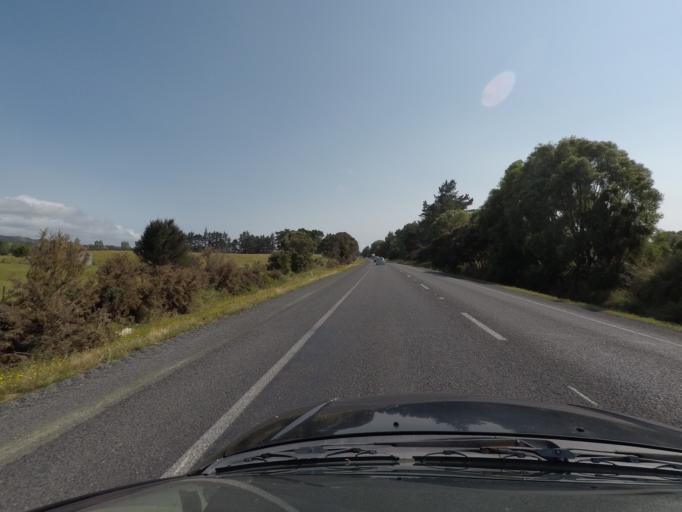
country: NZ
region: Northland
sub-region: Whangarei
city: Ruakaka
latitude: -35.9593
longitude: 174.4495
